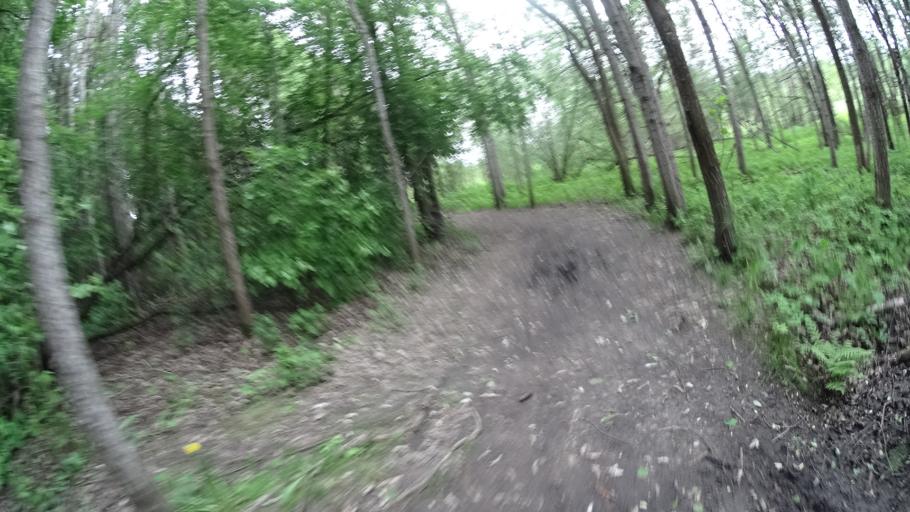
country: FI
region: Uusimaa
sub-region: Helsinki
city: Vantaa
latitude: 60.2783
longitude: 25.0578
